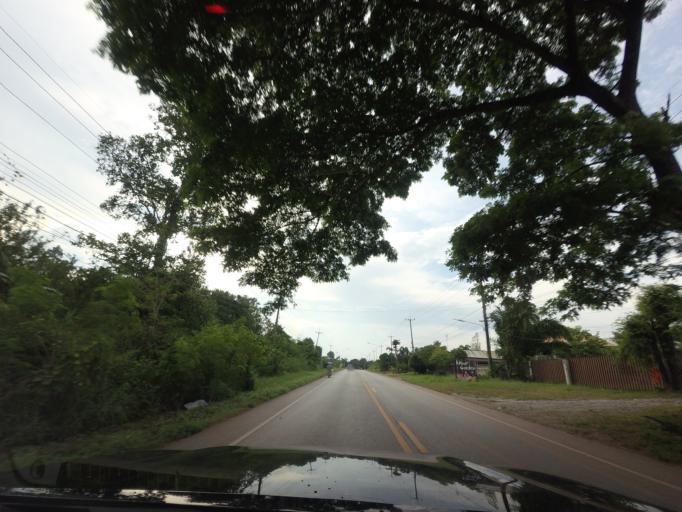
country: TH
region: Changwat Udon Thani
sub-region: Amphoe Ban Phue
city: Ban Phue
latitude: 17.7028
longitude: 102.4360
